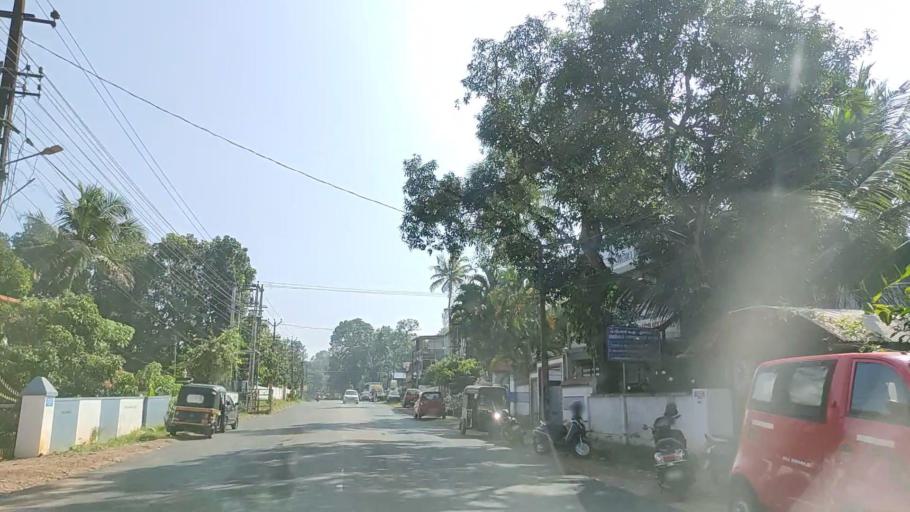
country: IN
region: Kerala
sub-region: Kollam
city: Punalur
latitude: 8.9271
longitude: 76.9218
